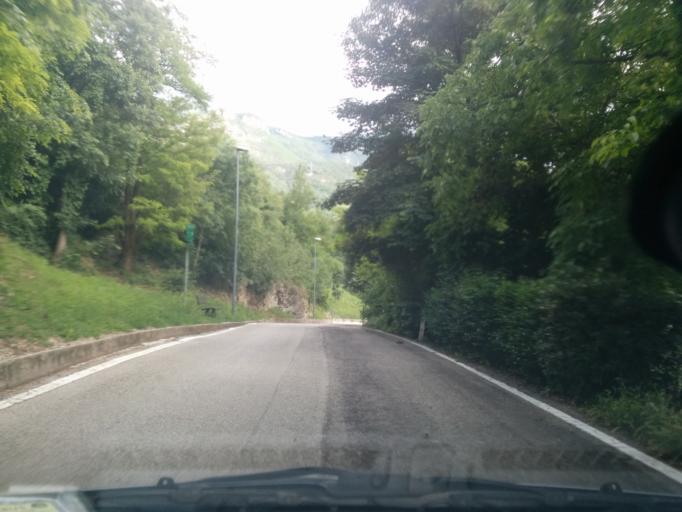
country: IT
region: Trentino-Alto Adige
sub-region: Provincia di Trento
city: Povo
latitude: 46.0722
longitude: 11.1408
